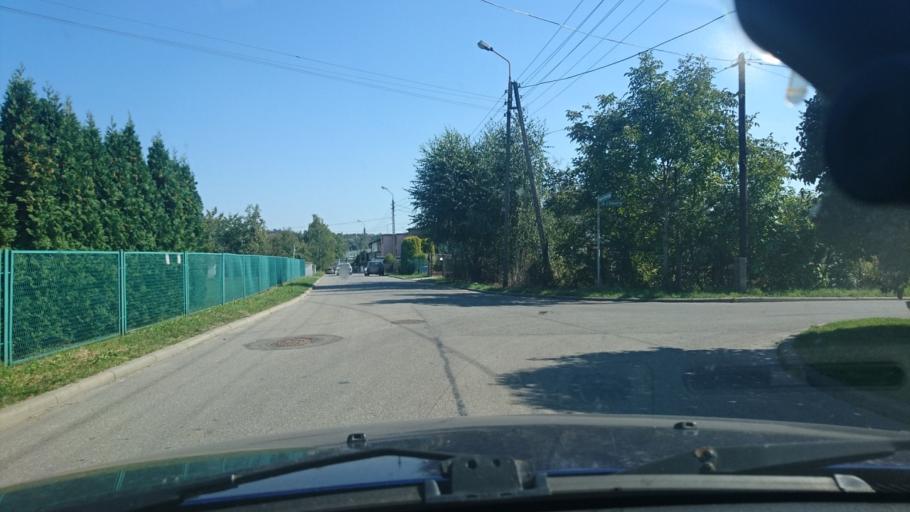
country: PL
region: Silesian Voivodeship
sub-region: Bielsko-Biala
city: Bielsko-Biala
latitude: 49.8441
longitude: 19.0642
